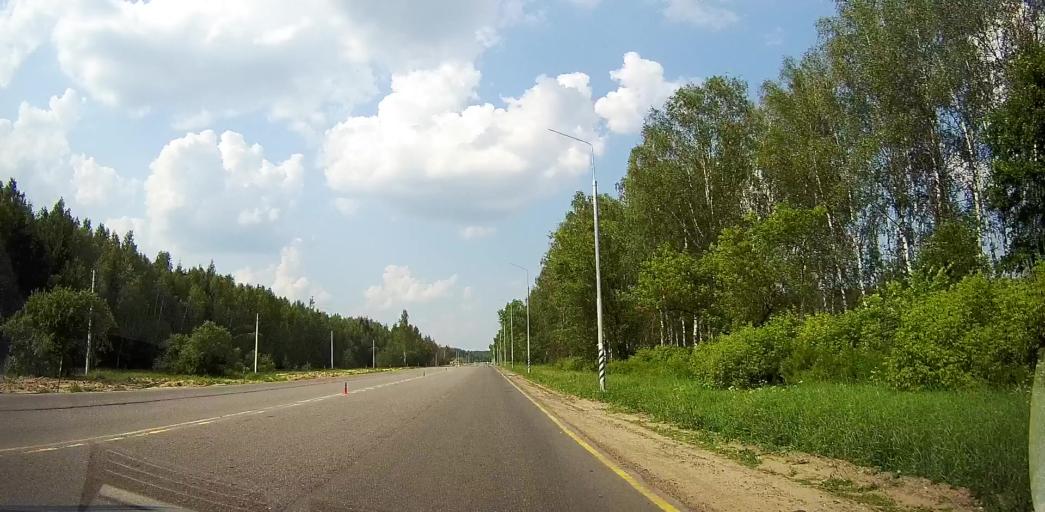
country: RU
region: Moskovskaya
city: Mikhnevo
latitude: 55.0662
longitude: 37.9533
